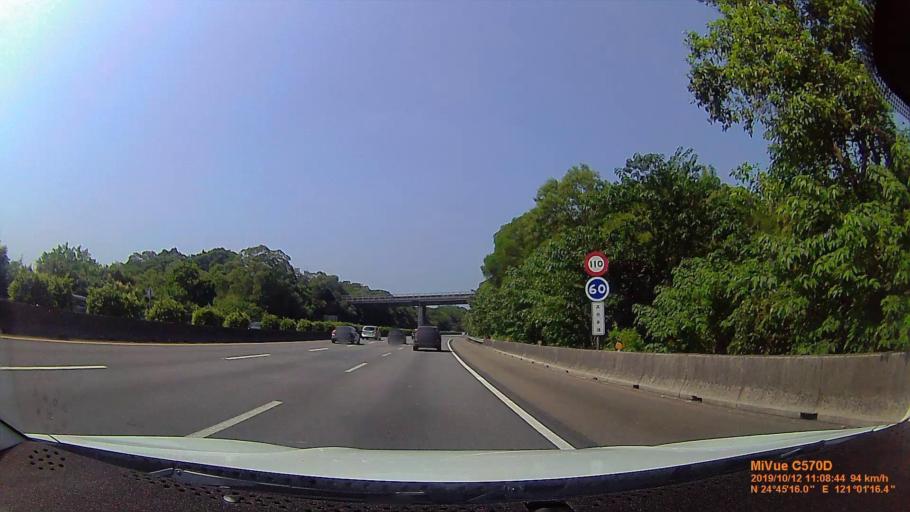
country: TW
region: Taiwan
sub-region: Hsinchu
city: Hsinchu
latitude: 24.7545
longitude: 121.0209
